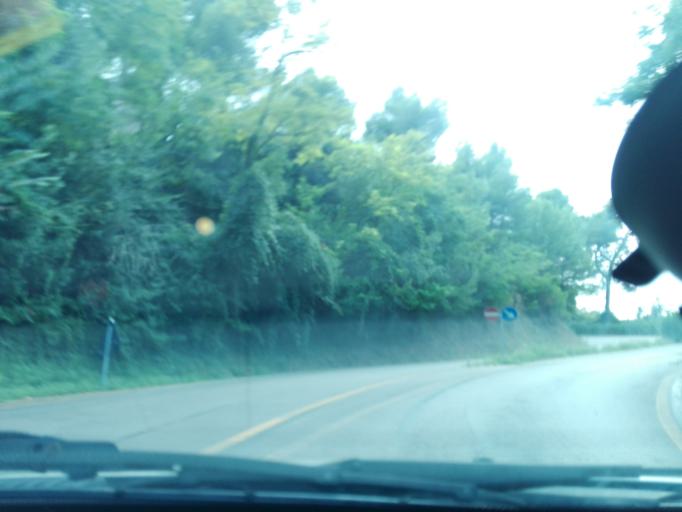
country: IT
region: Abruzzo
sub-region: Provincia di Pescara
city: Montesilvano Marina
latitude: 42.4916
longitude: 14.1436
